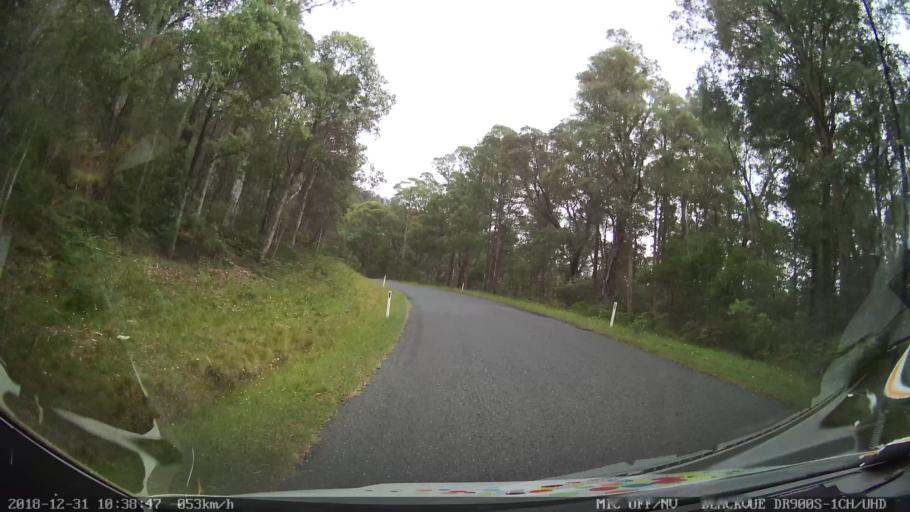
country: AU
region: New South Wales
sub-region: Snowy River
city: Jindabyne
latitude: -36.4042
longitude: 148.1779
